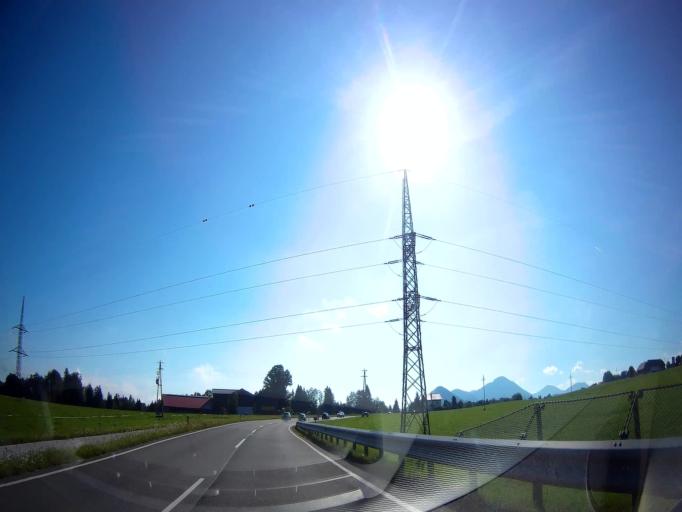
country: AT
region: Salzburg
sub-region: Politischer Bezirk Salzburg-Umgebung
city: Koppl
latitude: 47.8238
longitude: 13.1446
